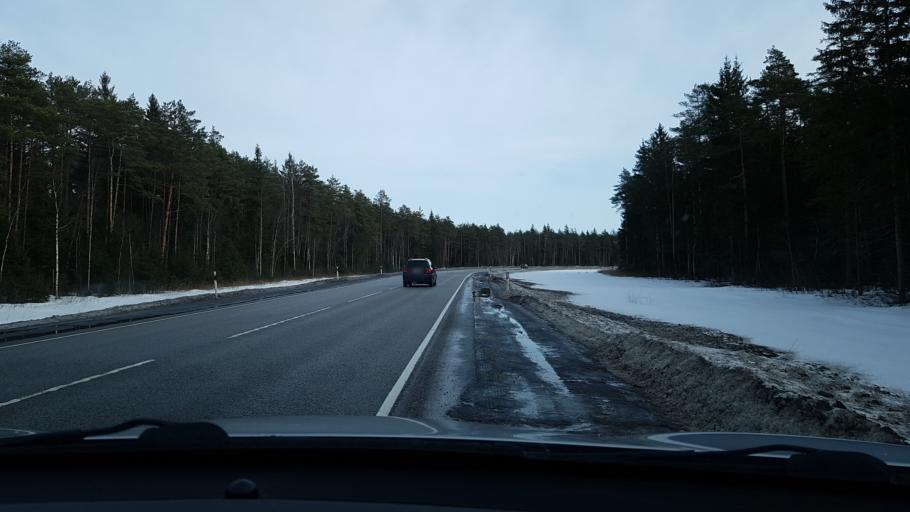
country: EE
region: Jaervamaa
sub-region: Paide linn
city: Paide
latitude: 59.0355
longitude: 25.5263
